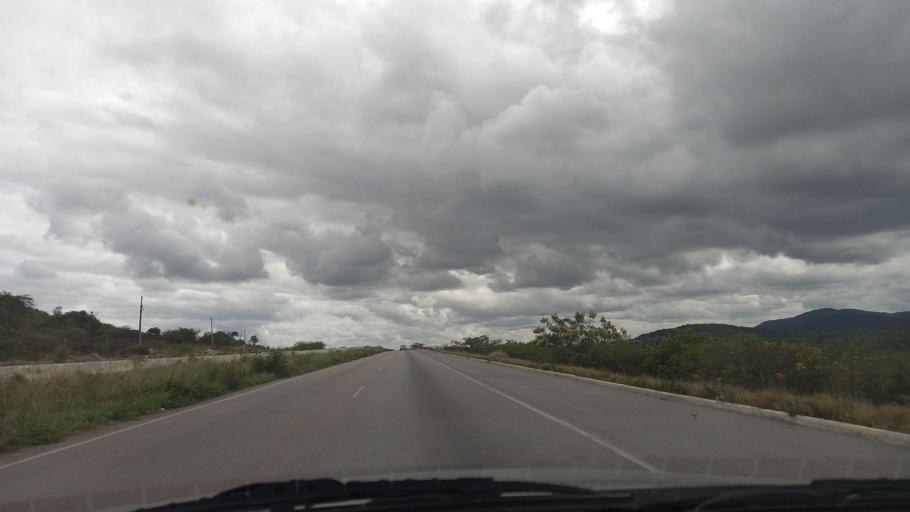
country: BR
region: Pernambuco
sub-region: Caruaru
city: Caruaru
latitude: -8.3237
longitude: -36.1067
